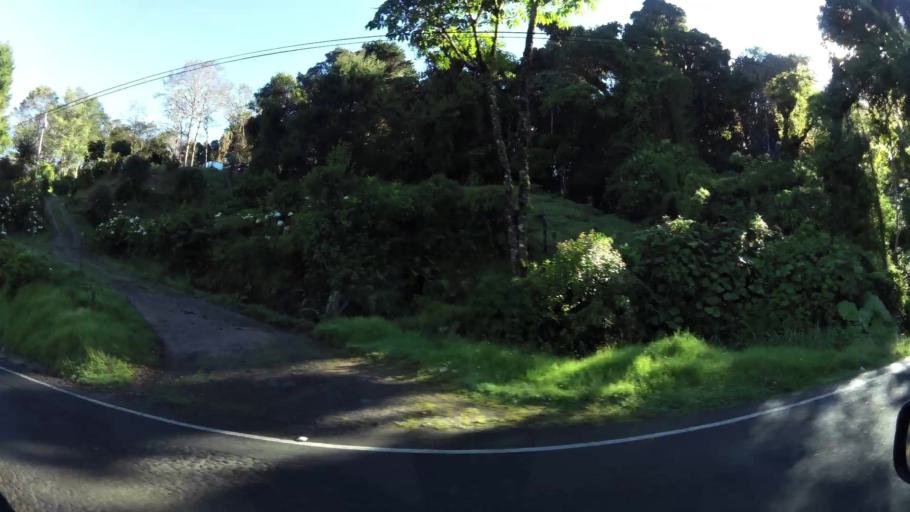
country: CR
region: San Jose
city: San Marcos
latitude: 9.7153
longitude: -83.9486
